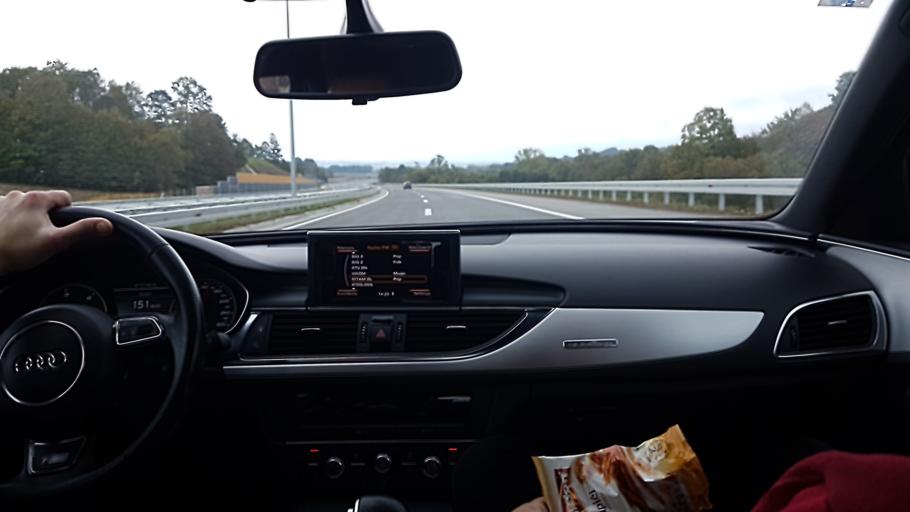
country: BA
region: Republika Srpska
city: Prnjavor
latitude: 44.8490
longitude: 17.7363
